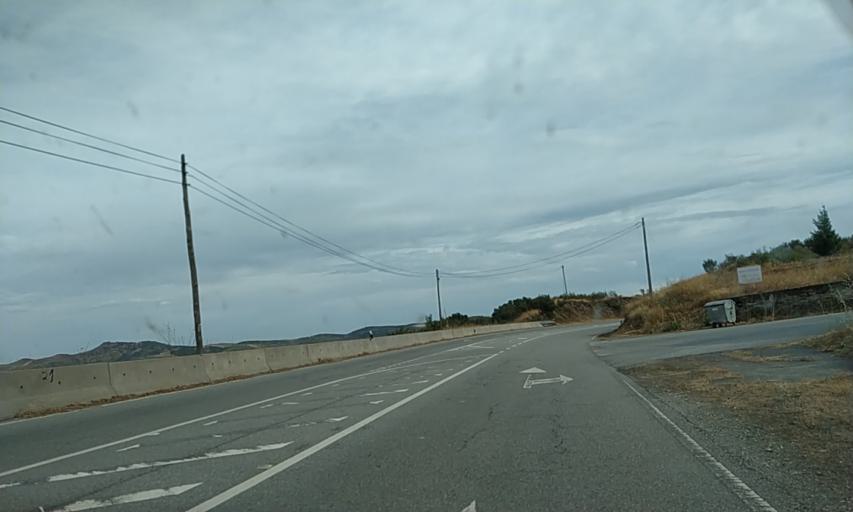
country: PT
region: Viseu
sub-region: Sao Joao da Pesqueira
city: Sao Joao da Pesqueira
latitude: 41.1166
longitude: -7.3868
